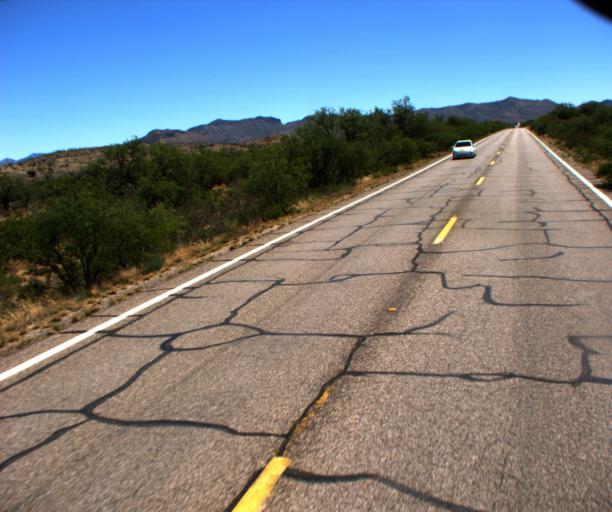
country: US
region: Arizona
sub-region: Pima County
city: Vail
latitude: 31.9666
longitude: -110.6734
